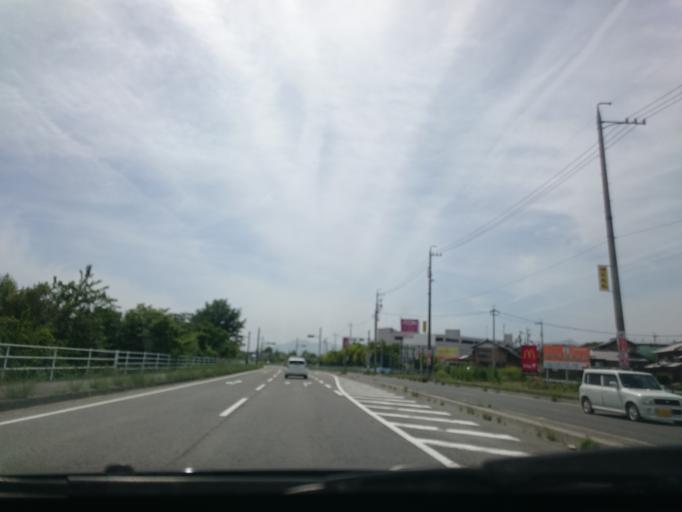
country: JP
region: Mie
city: Yokkaichi
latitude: 34.9769
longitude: 136.5950
